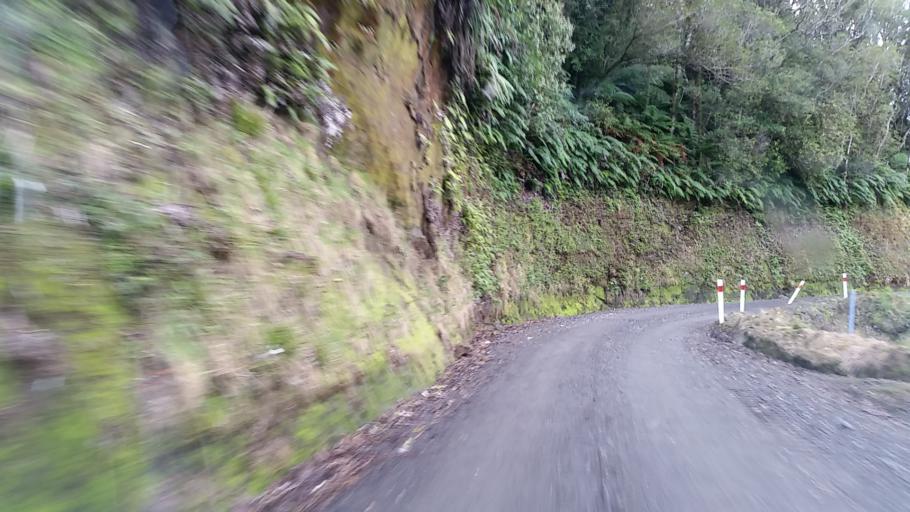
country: NZ
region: Taranaki
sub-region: New Plymouth District
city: Waitara
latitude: -39.1624
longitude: 174.5480
